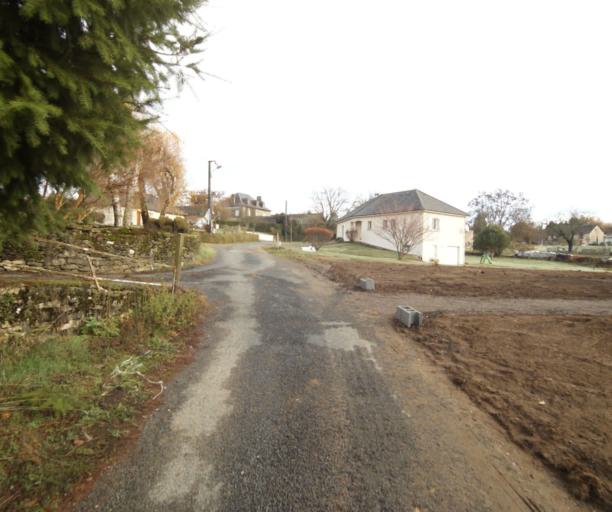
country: FR
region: Limousin
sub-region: Departement de la Correze
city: Cornil
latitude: 45.2129
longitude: 1.7109
